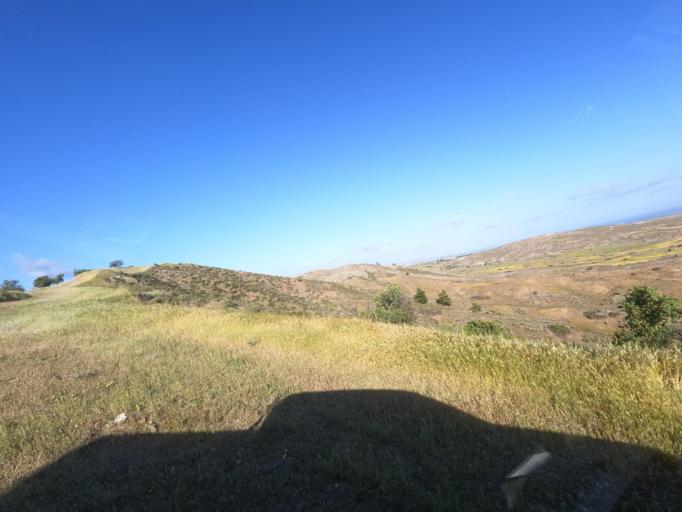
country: CY
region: Lefkosia
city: Astromeritis
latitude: 35.0725
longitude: 33.0399
